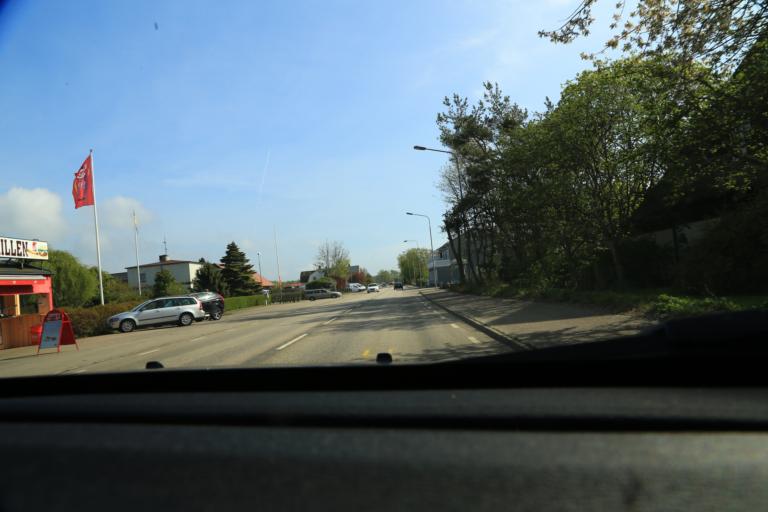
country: SE
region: Halland
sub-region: Varbergs Kommun
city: Veddige
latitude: 57.2202
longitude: 12.2217
